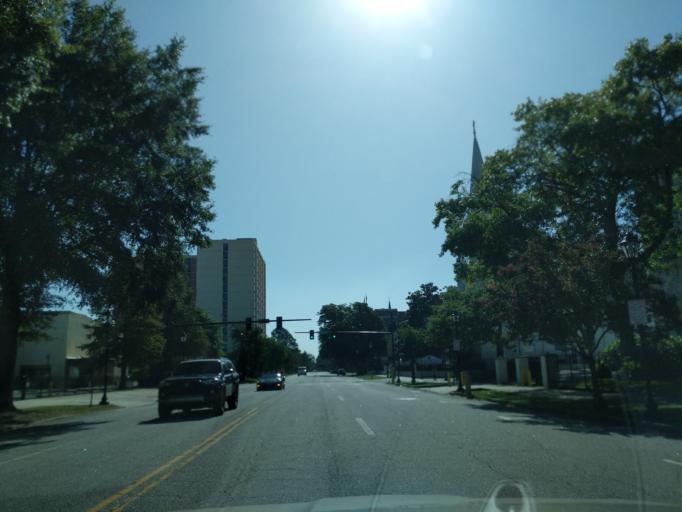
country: US
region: Georgia
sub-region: Richmond County
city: Augusta
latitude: 33.4723
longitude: -81.9677
